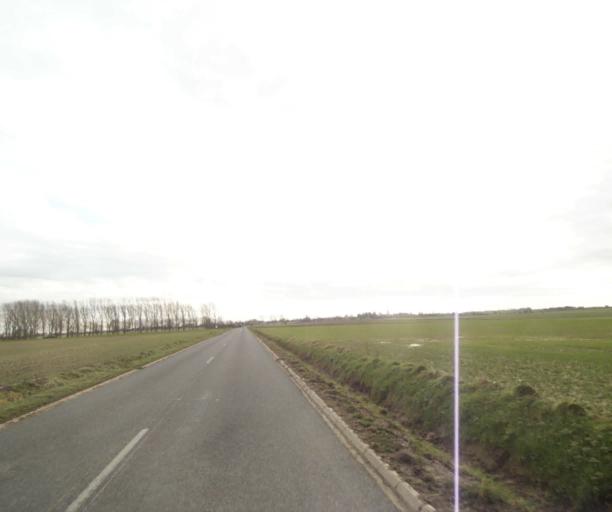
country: FR
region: Nord-Pas-de-Calais
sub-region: Departement du Nord
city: Quarouble
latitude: 50.3763
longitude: 3.6321
